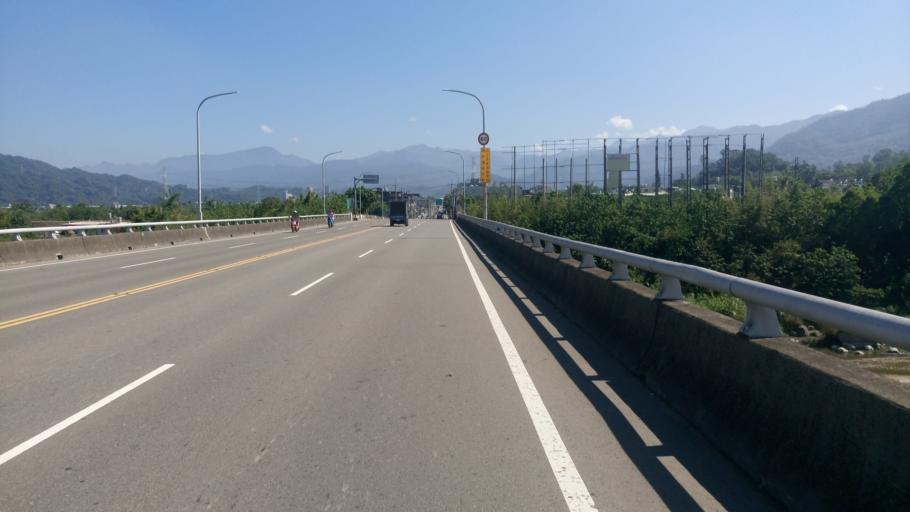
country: TW
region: Taiwan
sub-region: Hsinchu
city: Zhubei
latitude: 24.7224
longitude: 121.1054
